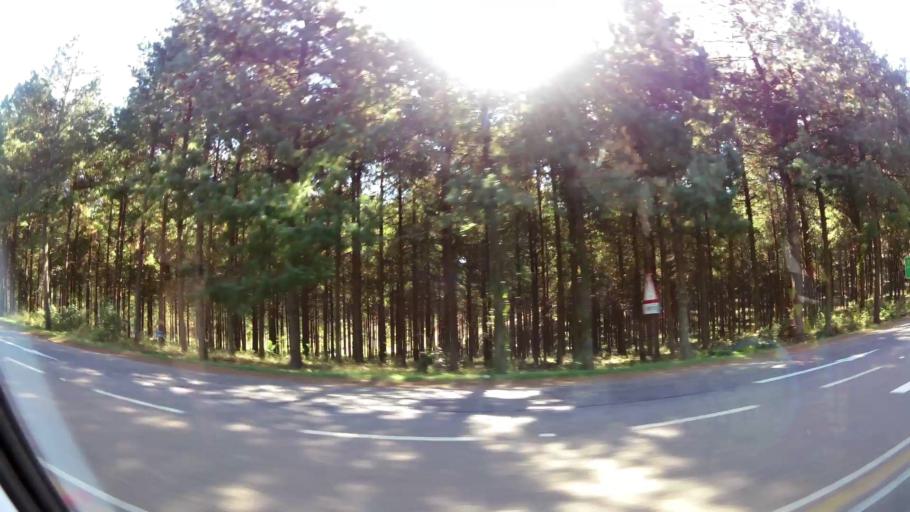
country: ZA
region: Limpopo
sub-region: Capricorn District Municipality
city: Mankoeng
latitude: -23.9273
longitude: 29.9605
